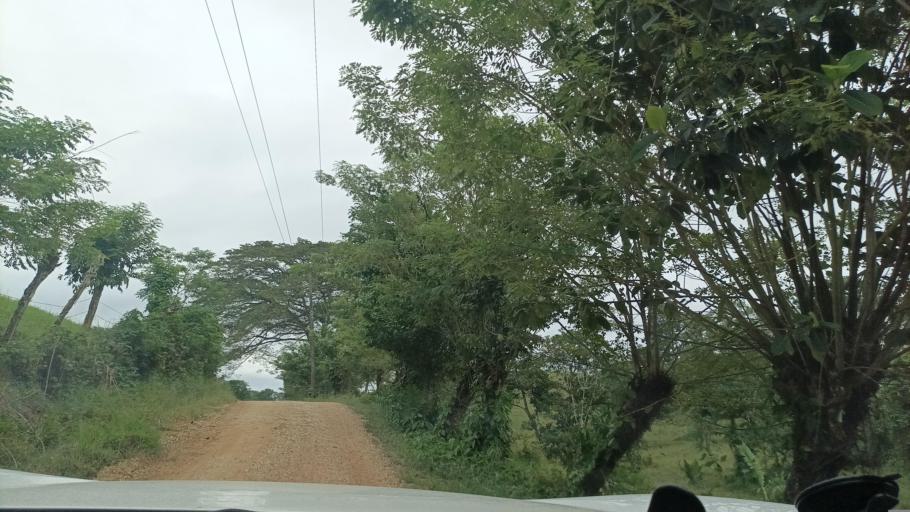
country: MX
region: Veracruz
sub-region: Uxpanapa
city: Poblado Cinco
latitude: 17.4908
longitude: -94.5690
